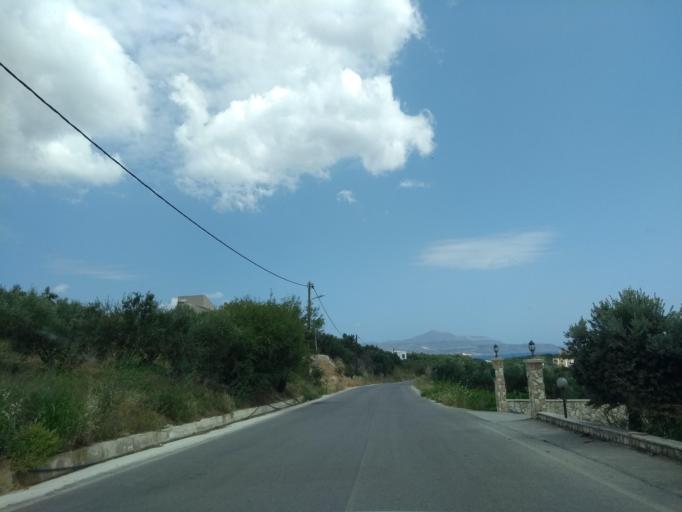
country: GR
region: Crete
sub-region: Nomos Chanias
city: Kalivai
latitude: 35.4391
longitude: 24.1755
